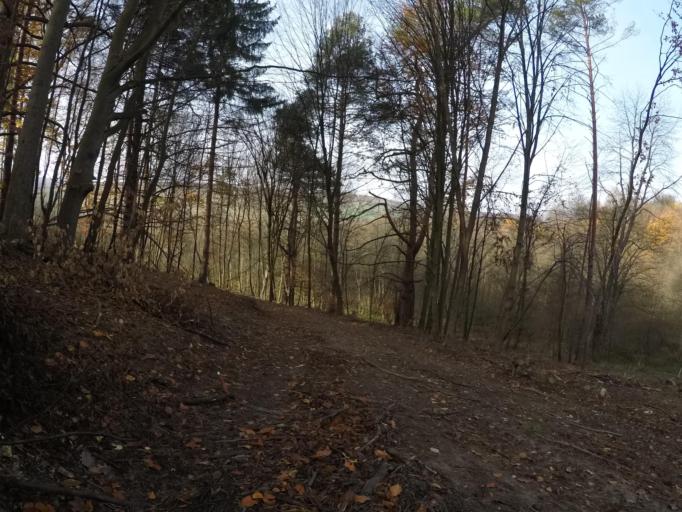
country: SK
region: Presovsky
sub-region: Okres Presov
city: Presov
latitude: 48.9163
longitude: 21.2062
